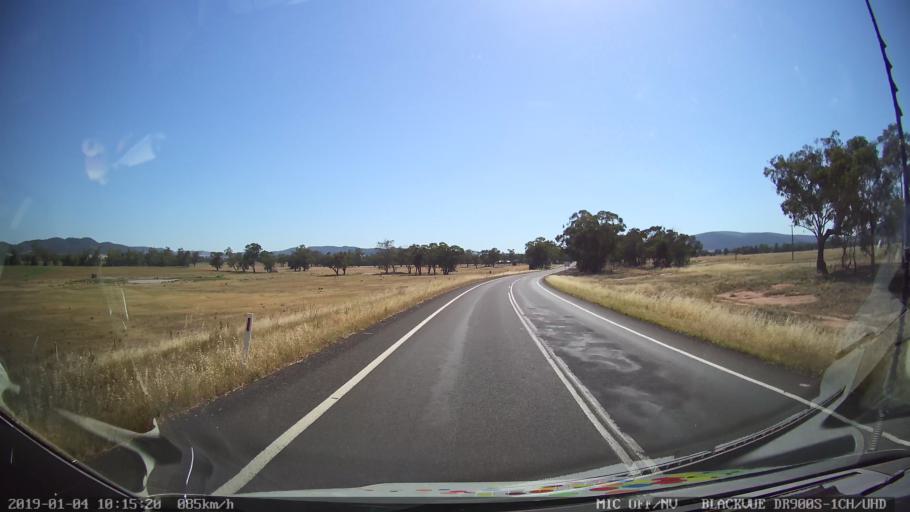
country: AU
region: New South Wales
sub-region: Cabonne
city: Canowindra
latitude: -33.3876
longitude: 148.4199
